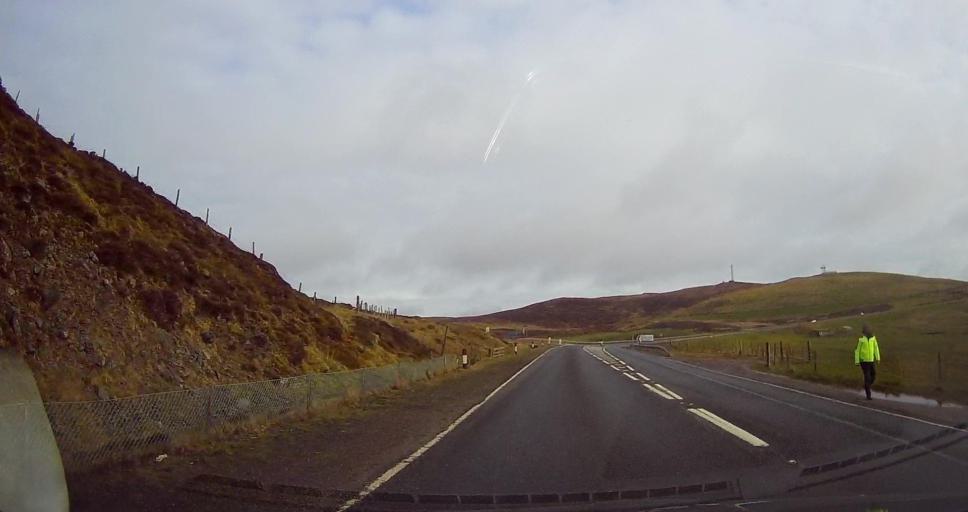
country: GB
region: Scotland
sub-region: Shetland Islands
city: Lerwick
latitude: 60.1351
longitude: -1.2144
